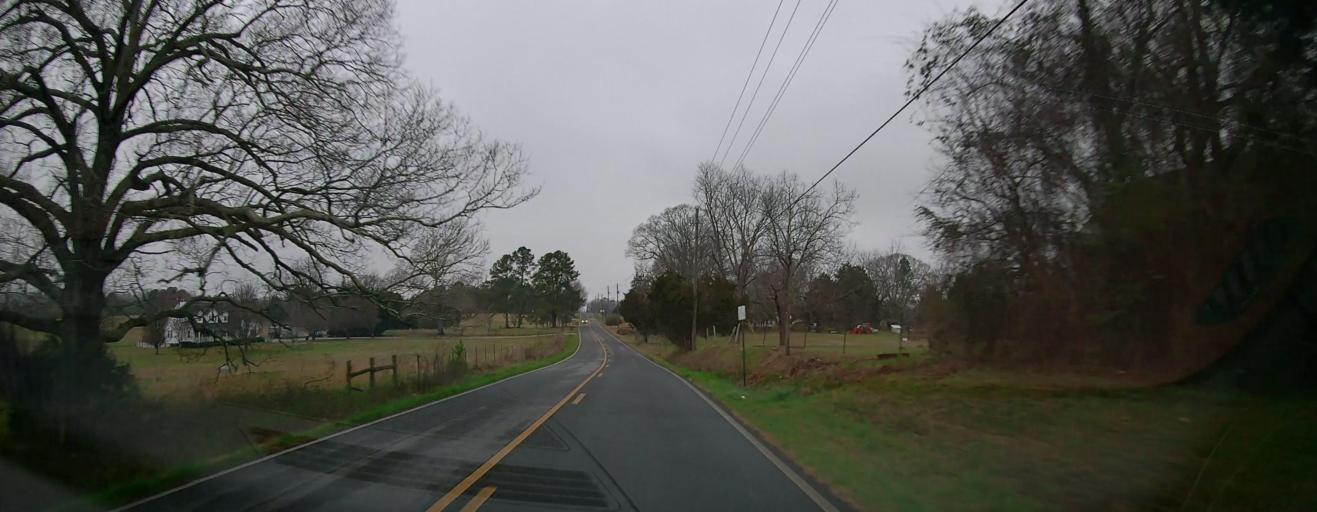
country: US
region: Georgia
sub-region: Pike County
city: Zebulon
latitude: 33.1460
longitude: -84.3474
